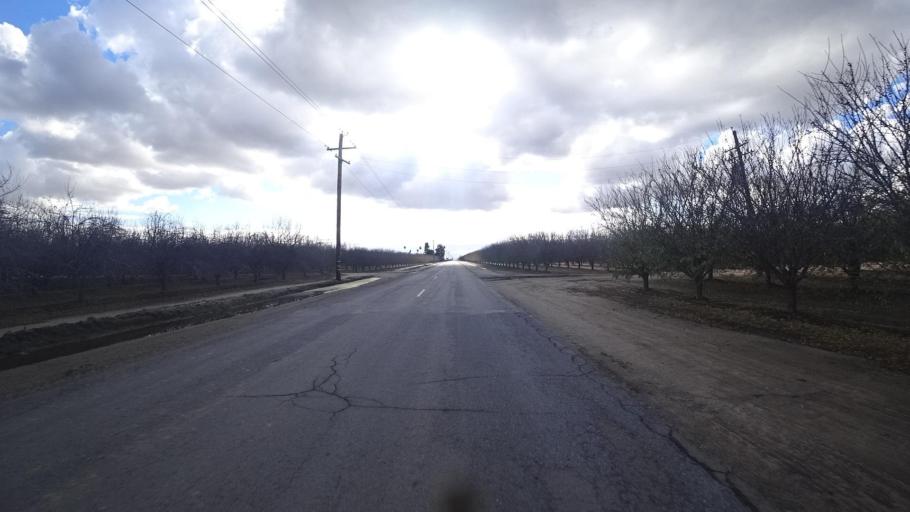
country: US
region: California
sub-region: Kern County
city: Greenfield
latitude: 35.2346
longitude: -119.0568
